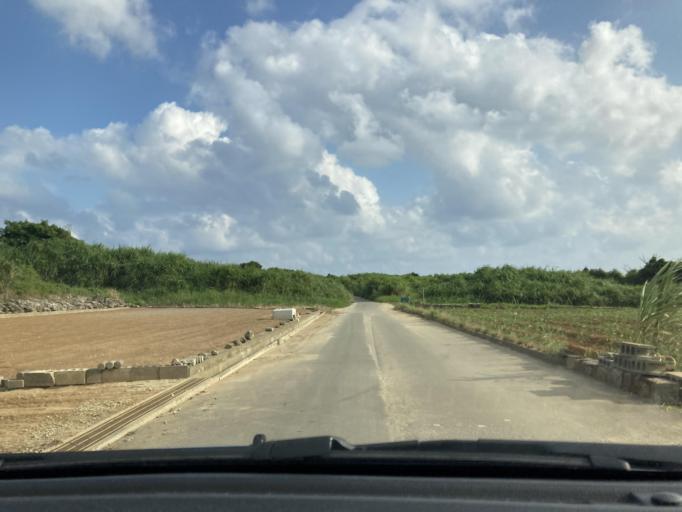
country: JP
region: Okinawa
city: Itoman
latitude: 26.0829
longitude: 127.6633
